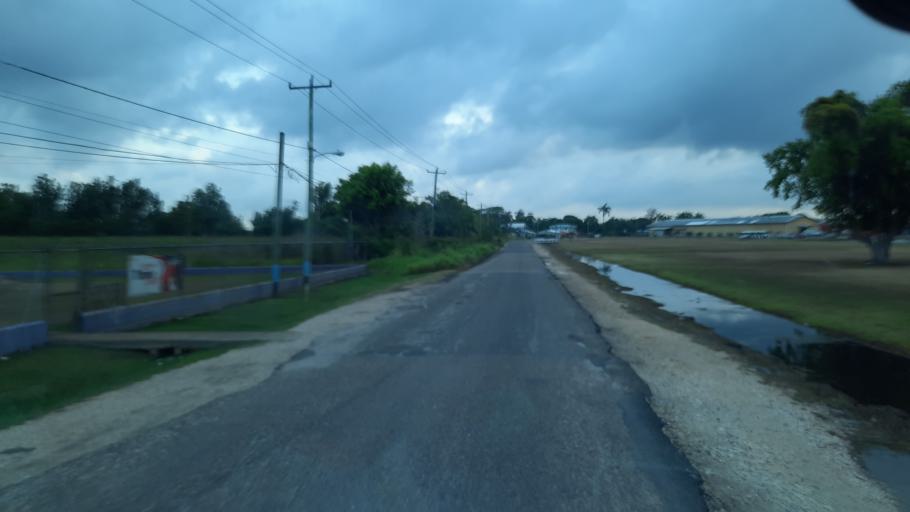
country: BZ
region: Belize
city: Belize City
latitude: 17.5468
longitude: -88.2957
